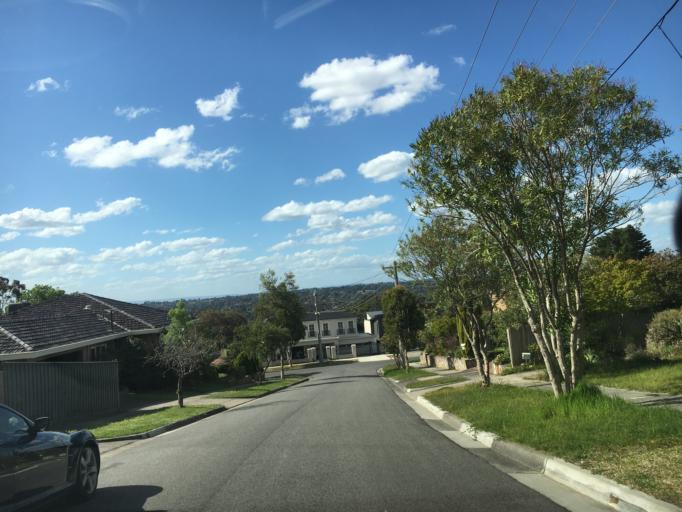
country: AU
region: Victoria
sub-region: Whitehorse
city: Vermont South
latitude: -37.8837
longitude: 145.1735
